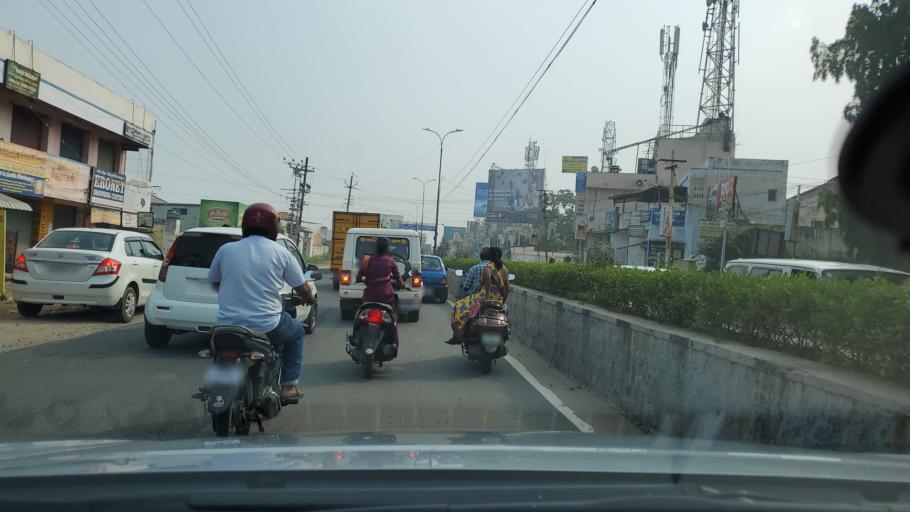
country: IN
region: Tamil Nadu
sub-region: Erode
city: Erode
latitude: 11.3351
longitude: 77.7082
